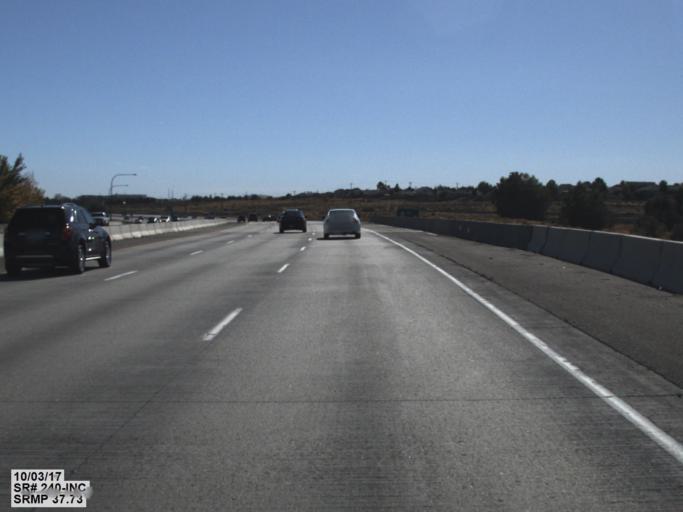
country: US
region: Washington
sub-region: Benton County
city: Richland
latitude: 46.2390
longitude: -119.2442
